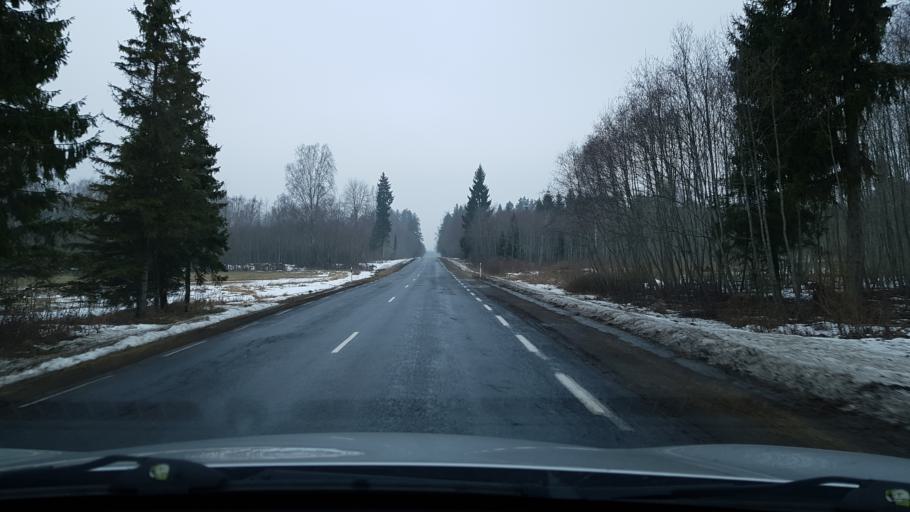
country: EE
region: Valgamaa
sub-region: Torva linn
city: Torva
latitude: 58.1750
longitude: 25.9602
